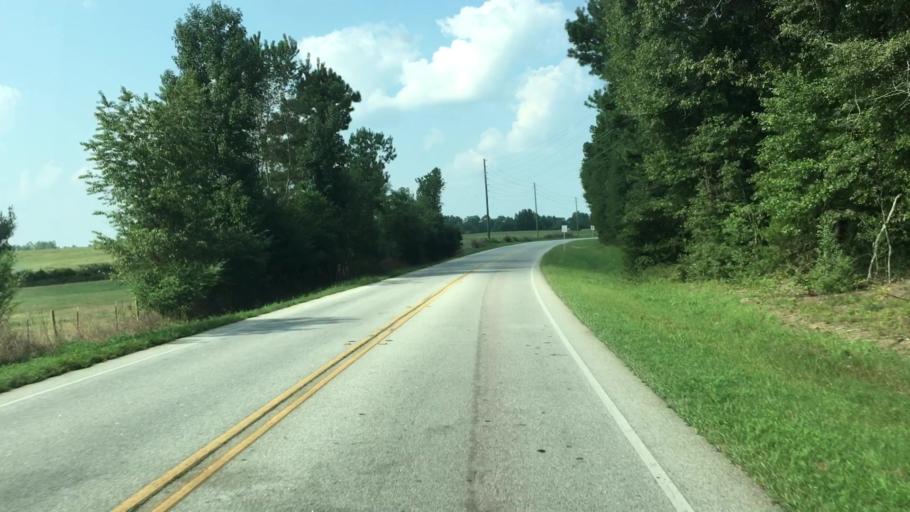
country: US
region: Georgia
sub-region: Newton County
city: Covington
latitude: 33.4688
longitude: -83.7535
